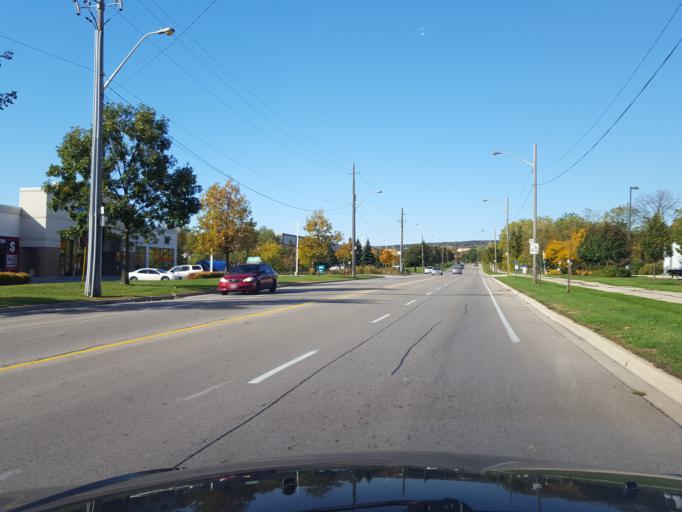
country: CA
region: Ontario
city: Burlington
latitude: 43.3453
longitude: -79.8185
